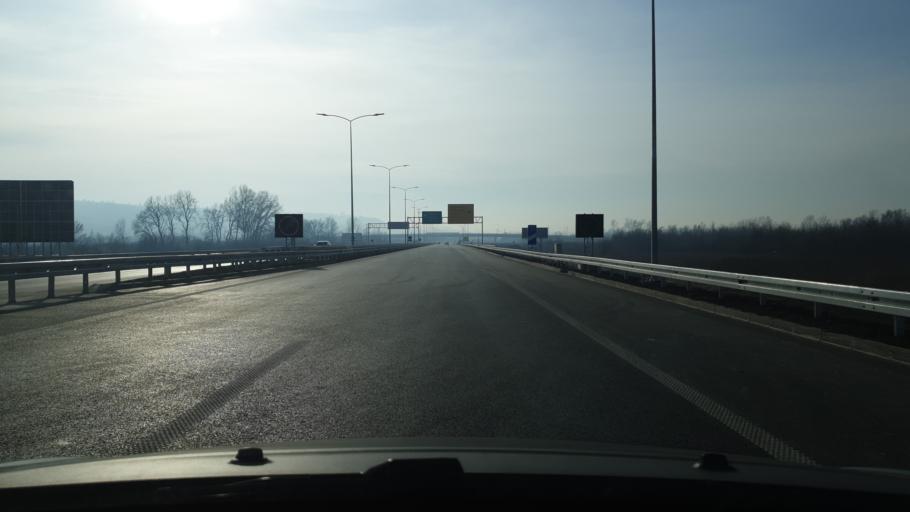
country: RS
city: Baric
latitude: 44.6569
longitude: 20.2367
